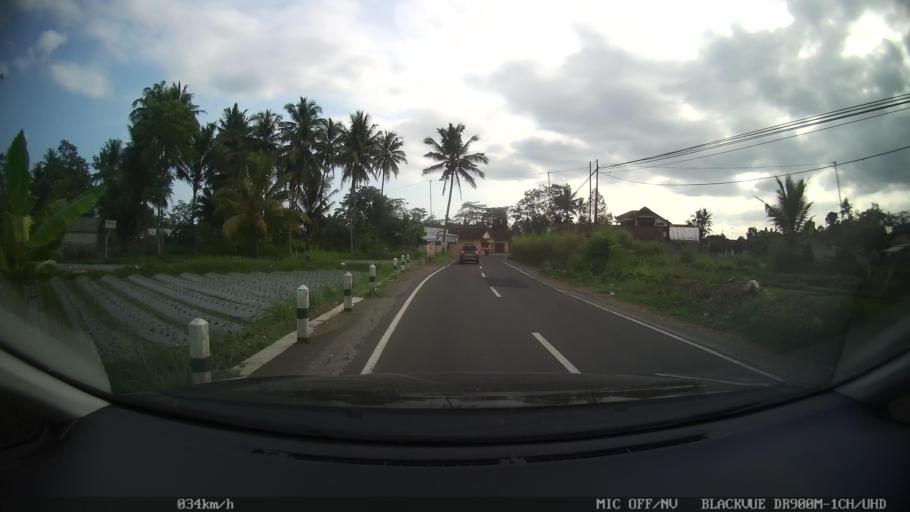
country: ID
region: Daerah Istimewa Yogyakarta
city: Depok
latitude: -7.6836
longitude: 110.4326
